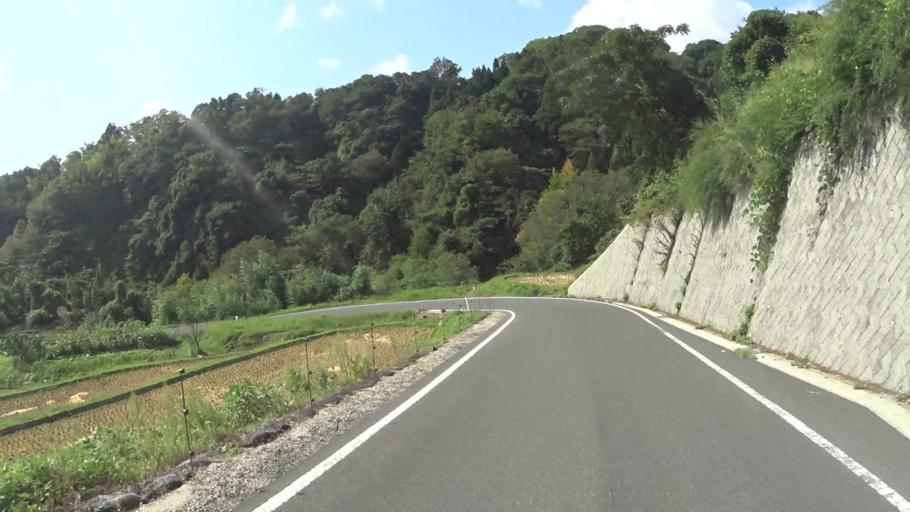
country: JP
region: Kyoto
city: Miyazu
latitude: 35.6371
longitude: 135.1901
